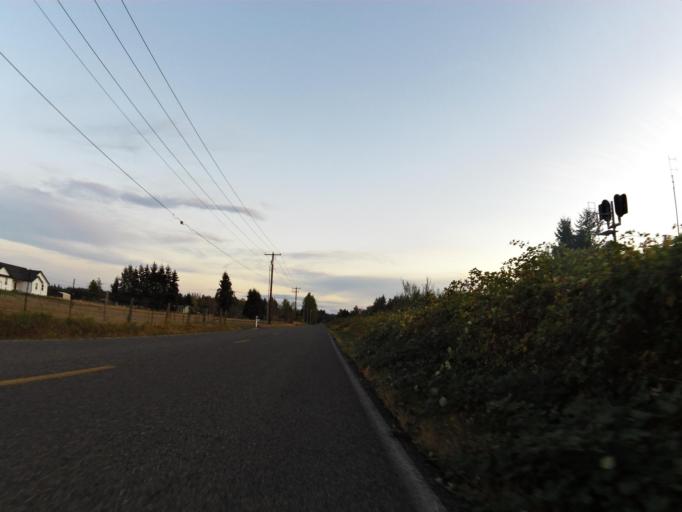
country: US
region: Washington
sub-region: Thurston County
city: Tenino
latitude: 46.8258
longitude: -122.8616
